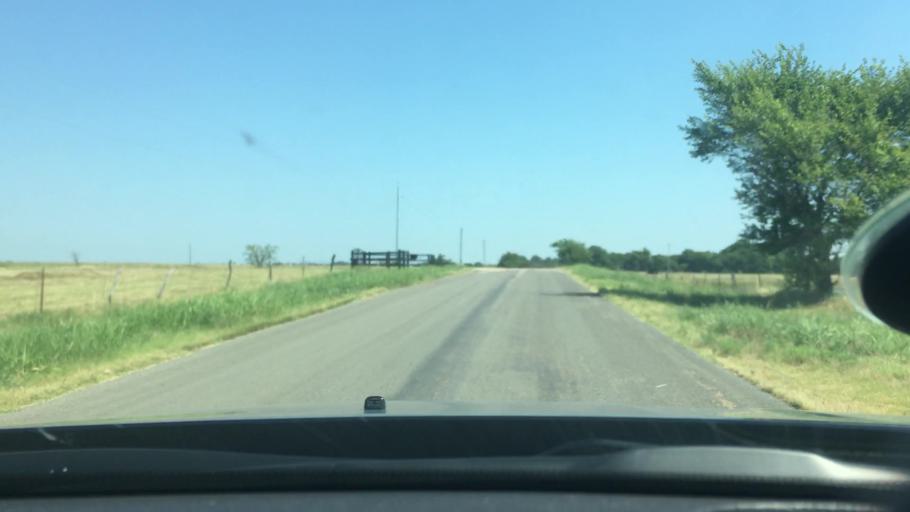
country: US
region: Oklahoma
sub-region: Johnston County
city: Tishomingo
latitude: 34.3151
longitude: -96.6360
